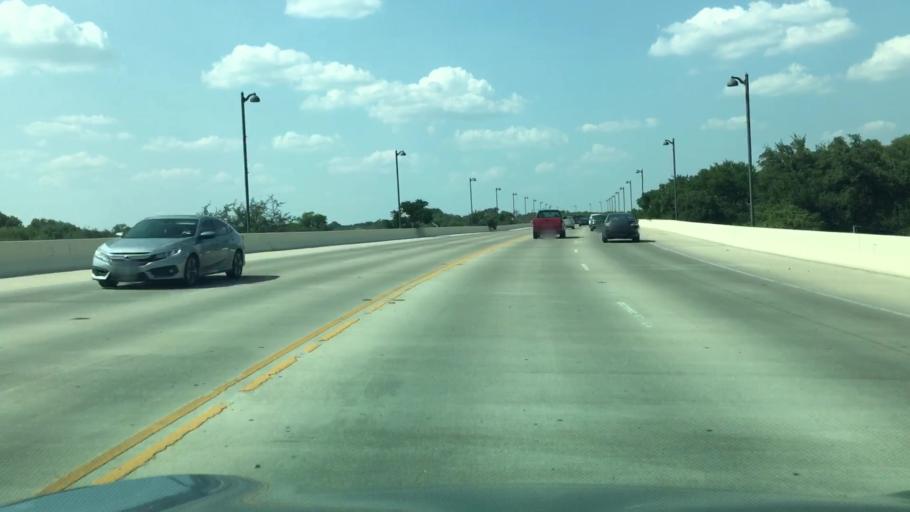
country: US
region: Texas
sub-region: Hays County
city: San Marcos
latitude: 29.8691
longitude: -97.9659
